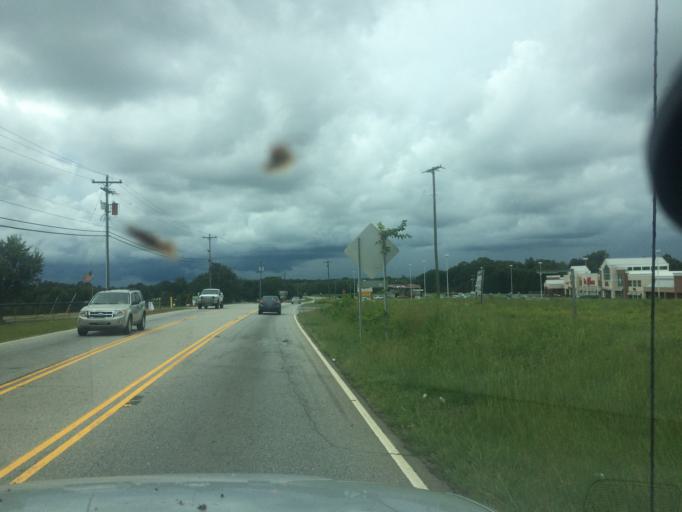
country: US
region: South Carolina
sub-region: Greenville County
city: Taylors
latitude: 34.9480
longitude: -82.2720
